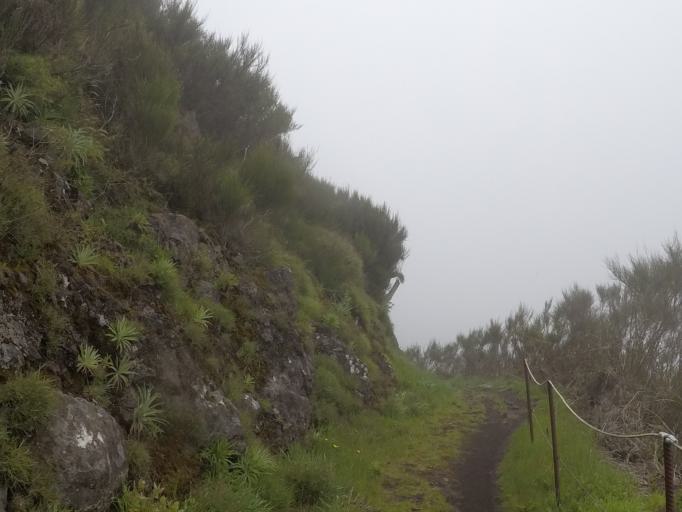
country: PT
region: Madeira
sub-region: Camara de Lobos
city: Curral das Freiras
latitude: 32.7248
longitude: -16.9882
